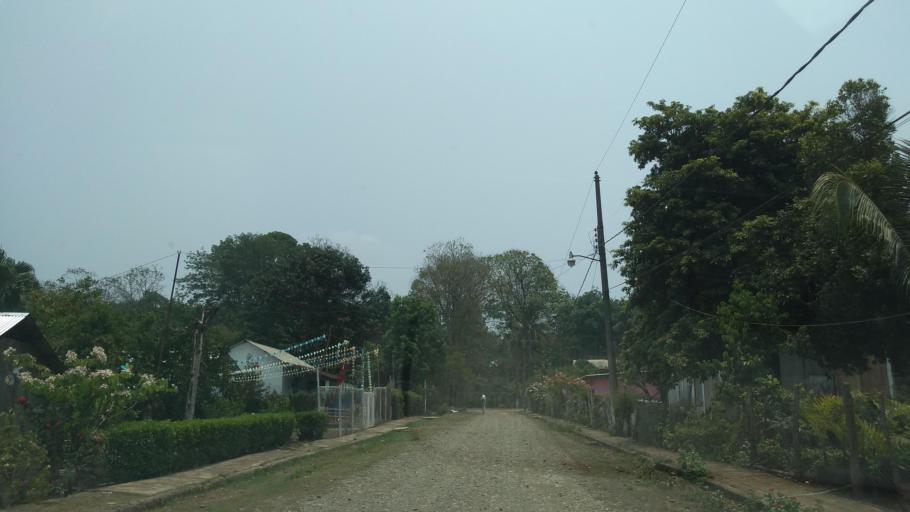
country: MX
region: Veracruz
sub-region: Tezonapa
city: Laguna Chica (Pueblo Nuevo)
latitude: 18.5142
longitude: -96.7632
